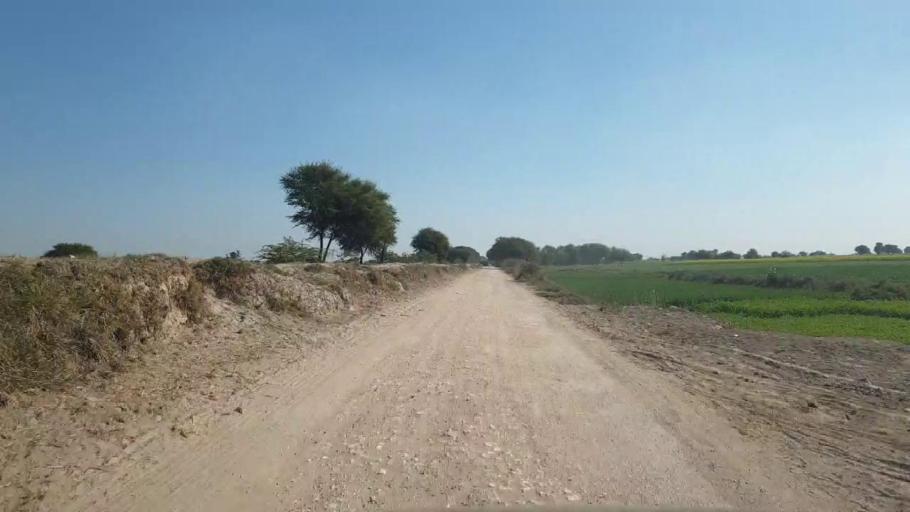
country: PK
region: Sindh
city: Shahpur Chakar
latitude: 26.1429
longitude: 68.6524
